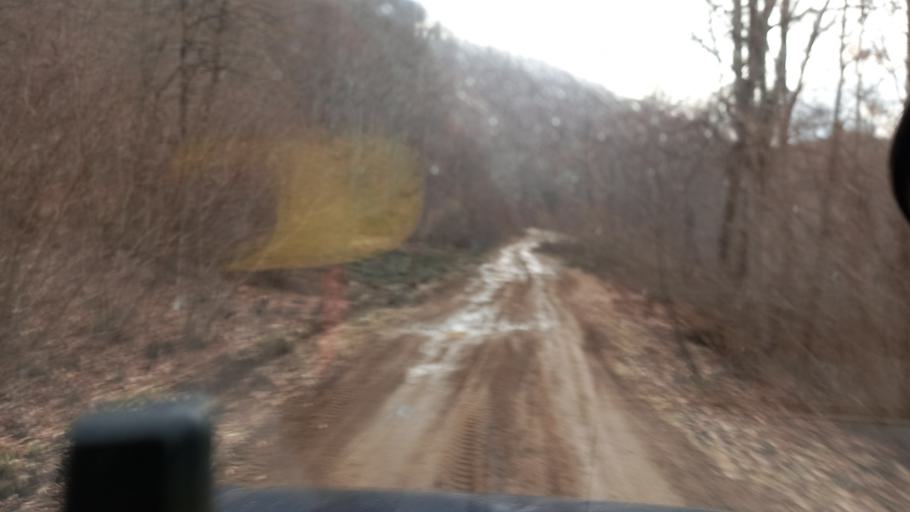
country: RU
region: Adygeya
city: Kamennomostskiy
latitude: 44.1760
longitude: 40.2999
